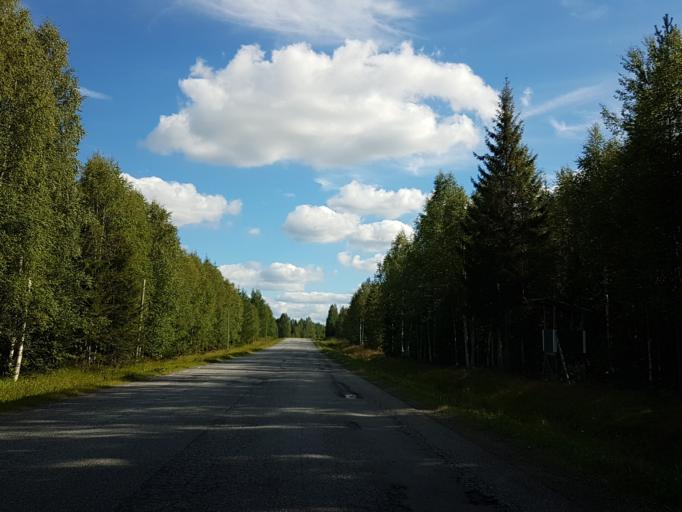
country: SE
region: Vaesterbotten
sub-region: Skelleftea Kommun
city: Burtraesk
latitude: 64.3257
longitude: 20.5280
